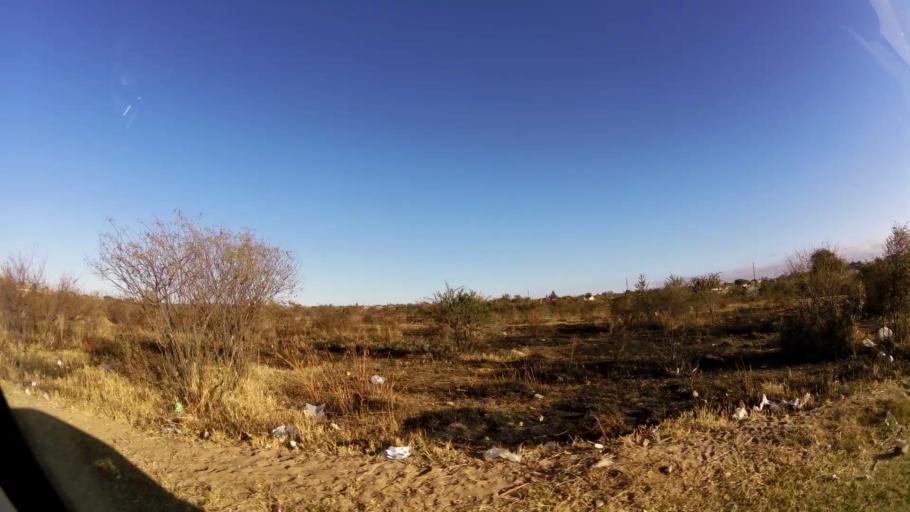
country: ZA
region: Limpopo
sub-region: Capricorn District Municipality
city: Polokwane
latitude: -23.8415
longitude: 29.3592
